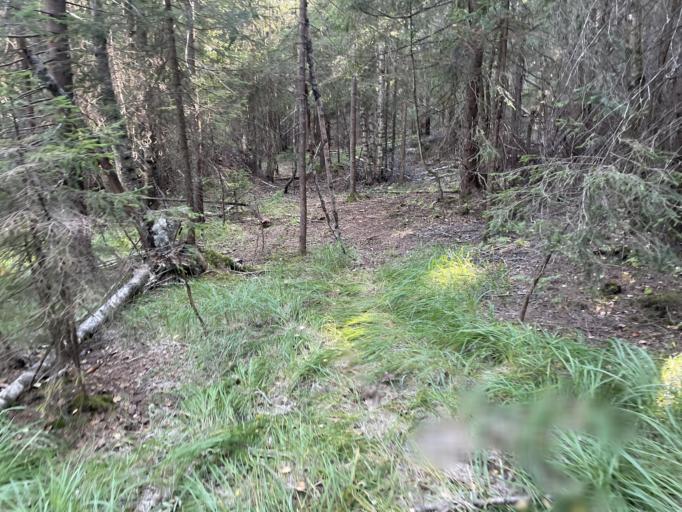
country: NO
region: Akershus
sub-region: Nittedal
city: Rotnes
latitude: 60.0630
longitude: 10.8257
